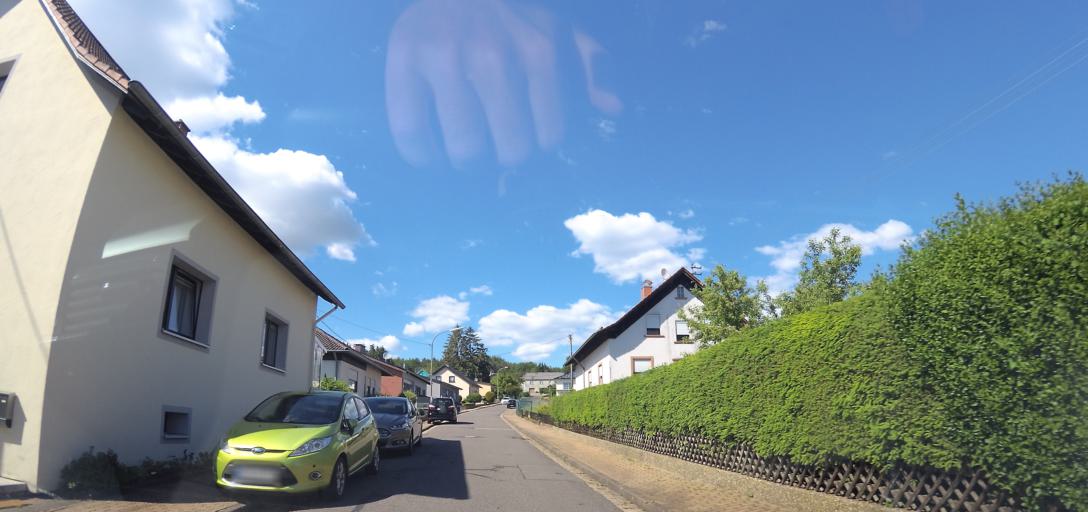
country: DE
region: Saarland
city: Weiskirchen
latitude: 49.5579
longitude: 6.8300
